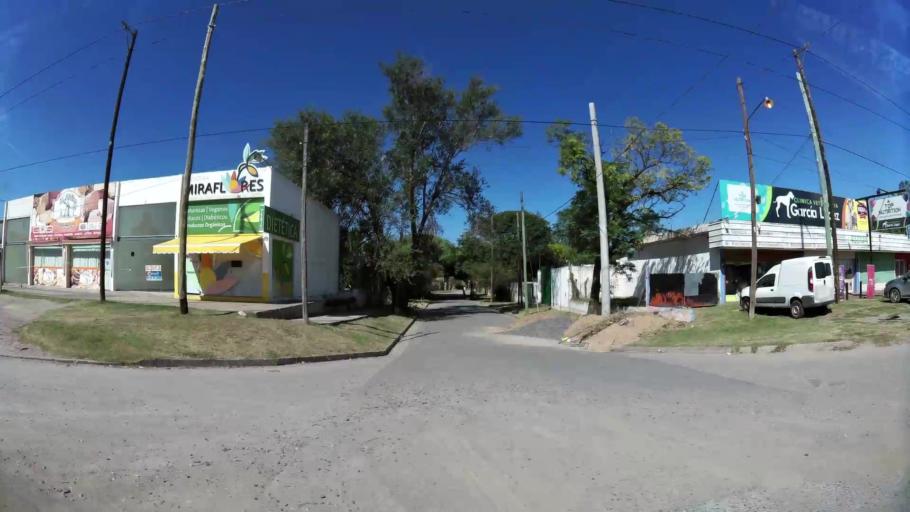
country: AR
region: Cordoba
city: Saldan
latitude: -31.3173
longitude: -64.2883
